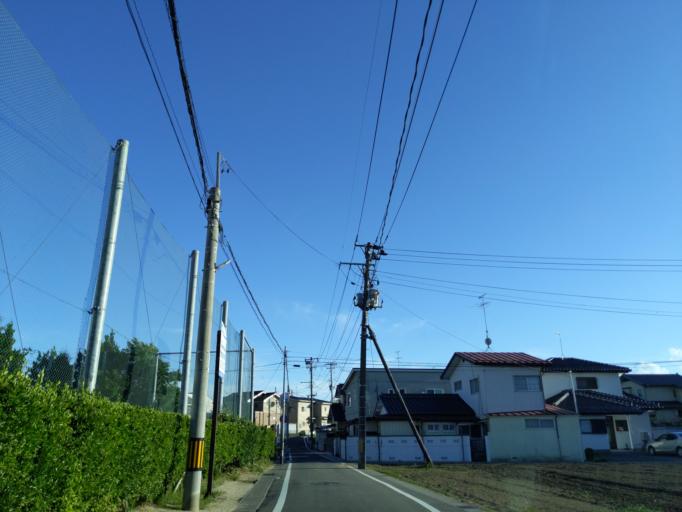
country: JP
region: Fukushima
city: Koriyama
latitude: 37.3913
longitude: 140.4060
